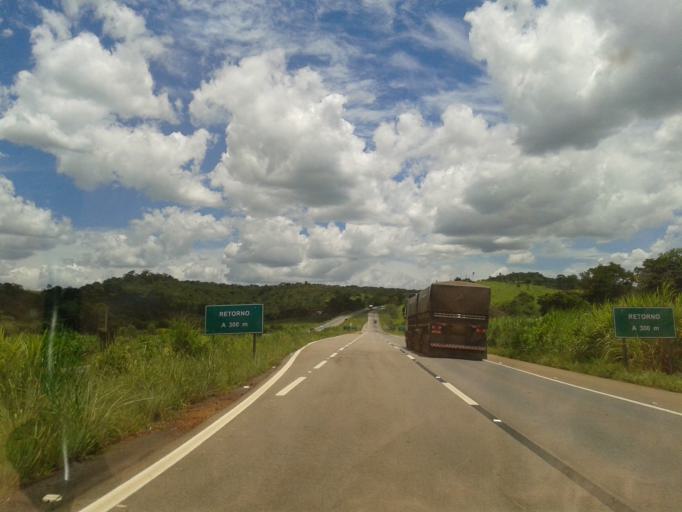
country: BR
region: Goias
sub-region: Neropolis
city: Neropolis
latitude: -16.3496
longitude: -49.2547
